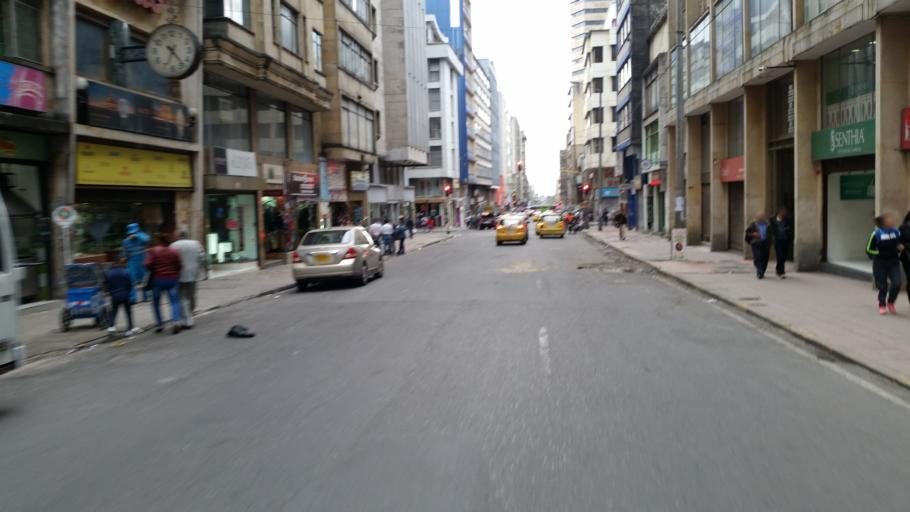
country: CO
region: Bogota D.C.
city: Bogota
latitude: 4.6036
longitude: -74.0723
